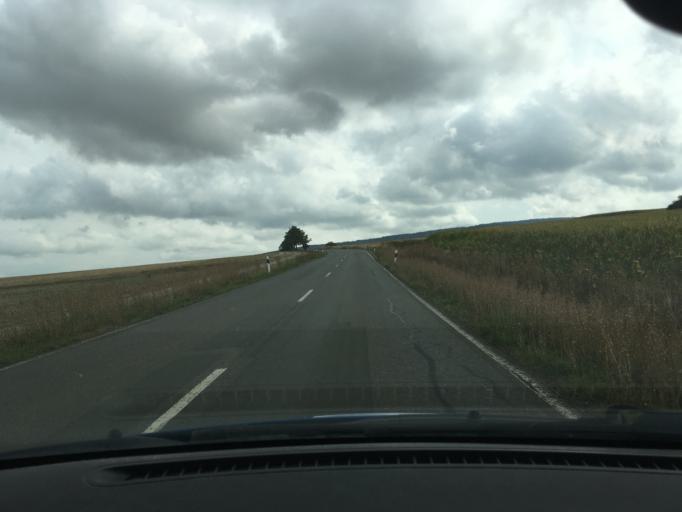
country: DE
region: Lower Saxony
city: Hulsede
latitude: 52.2200
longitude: 9.3856
